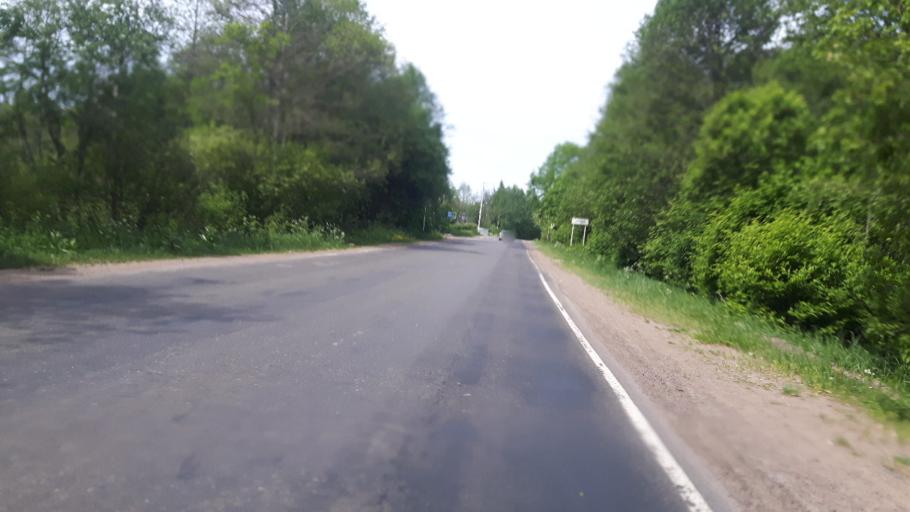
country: RU
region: Leningrad
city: Ust'-Luga
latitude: 59.6390
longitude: 28.2817
